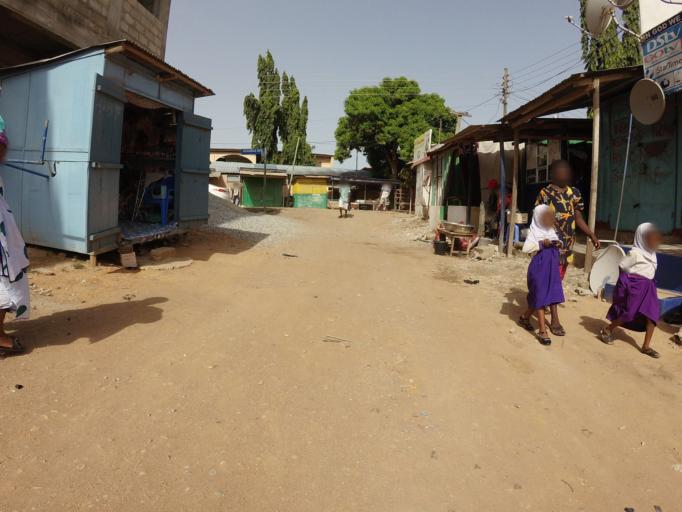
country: GH
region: Greater Accra
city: Dome
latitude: 5.6141
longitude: -0.2404
